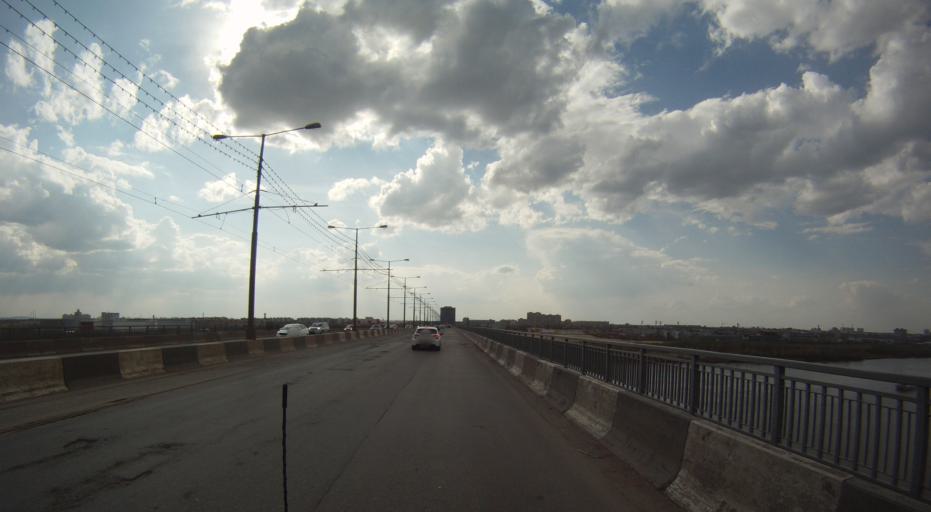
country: RU
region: Nizjnij Novgorod
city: Nizhniy Novgorod
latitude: 56.2989
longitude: 43.9657
